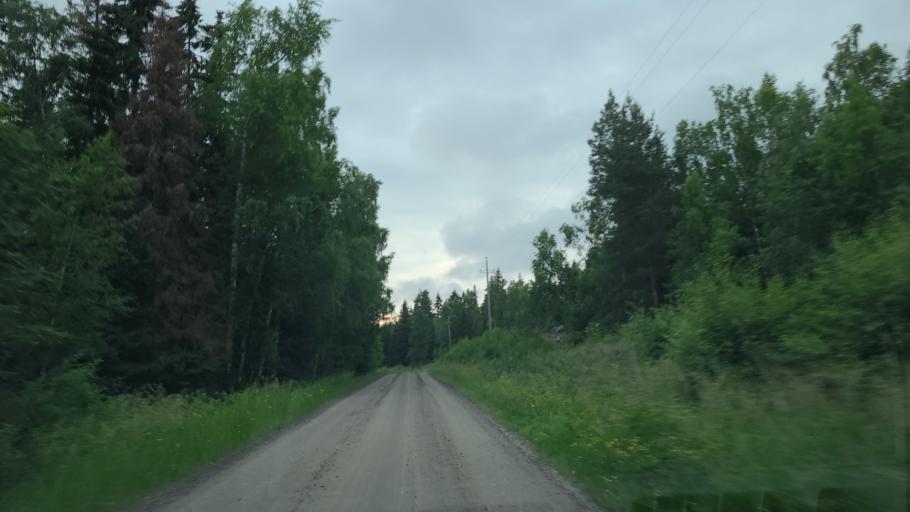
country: FI
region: Ostrobothnia
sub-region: Vaasa
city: Replot
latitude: 63.3147
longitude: 21.1592
